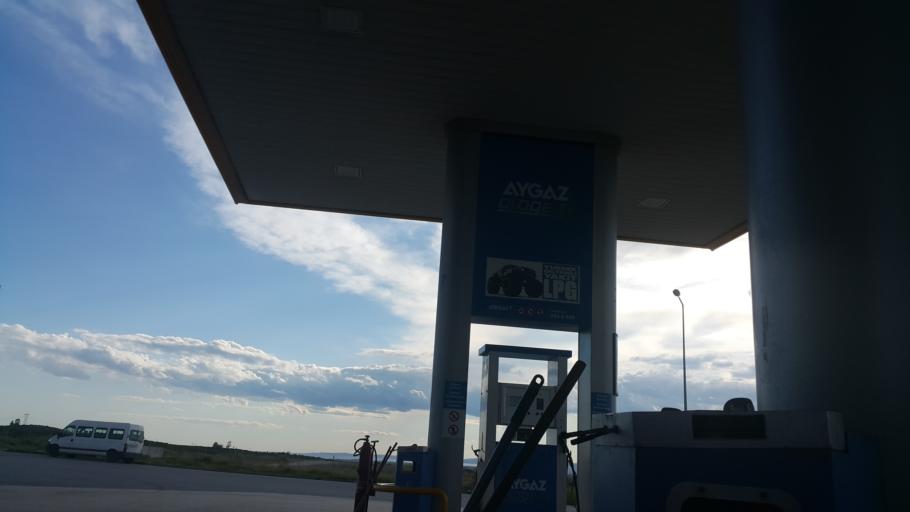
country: TR
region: Hatay
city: Mahmutlar
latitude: 36.9531
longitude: 36.1586
